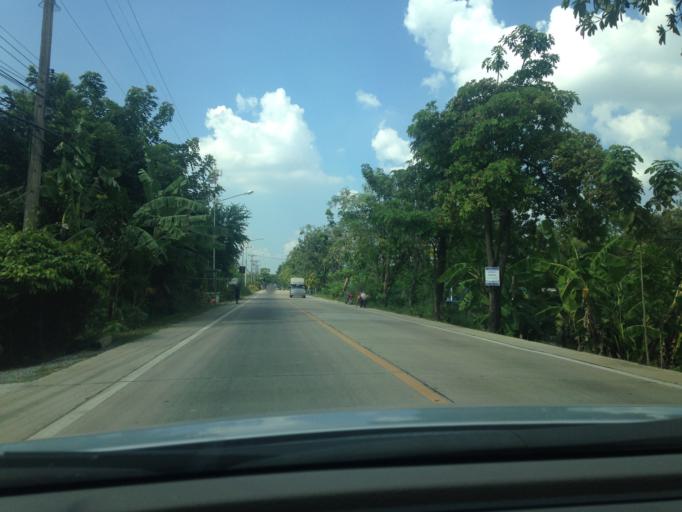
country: TH
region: Pathum Thani
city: Khlong Luang
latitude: 14.0499
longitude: 100.5907
